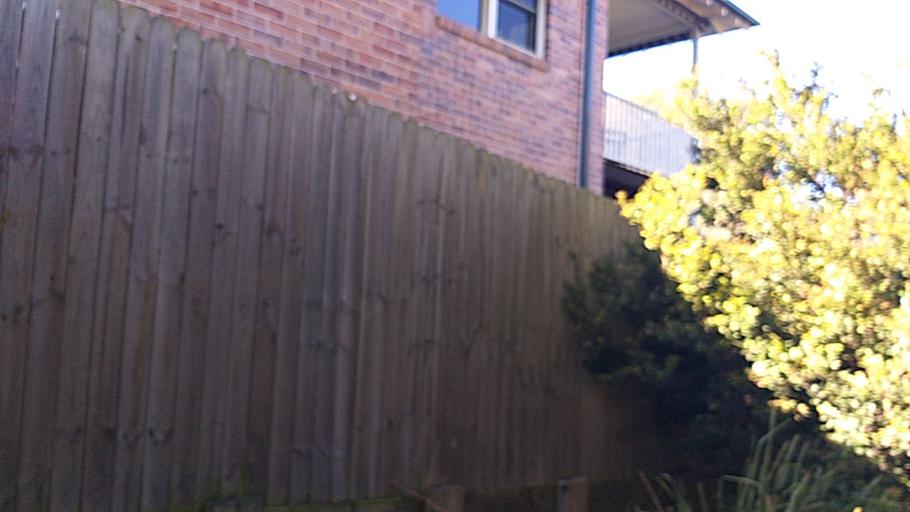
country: AU
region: New South Wales
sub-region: Hunters Hill
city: Gladesville
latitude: -33.8241
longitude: 151.1169
